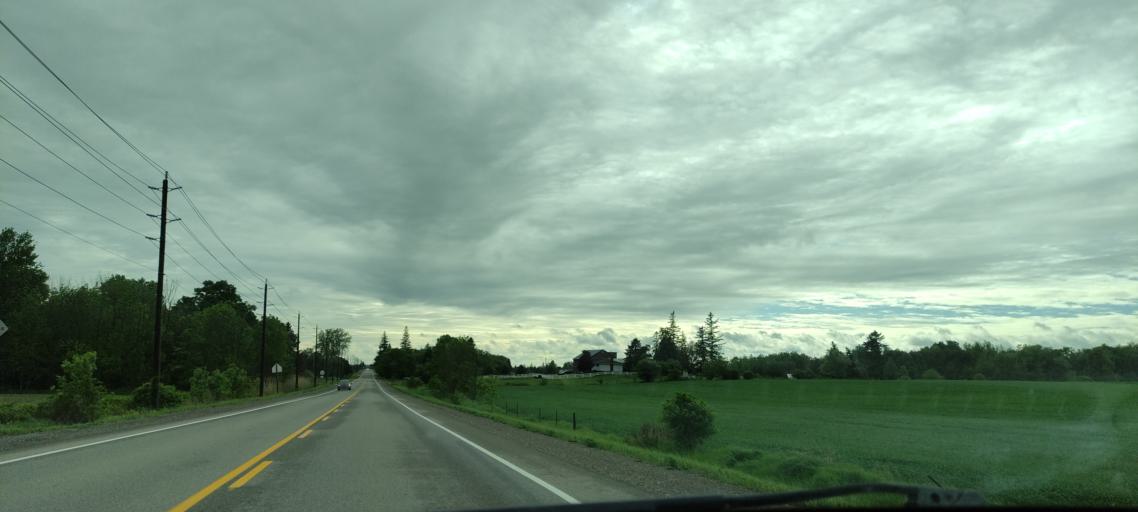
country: CA
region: Ontario
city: Kitchener
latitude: 43.3853
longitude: -80.6307
